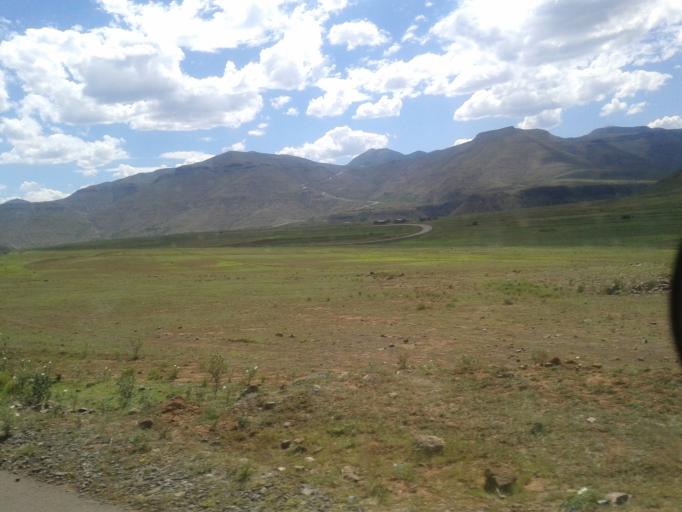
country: LS
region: Qacha's Nek
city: Qacha's Nek
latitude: -30.0254
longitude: 28.2066
